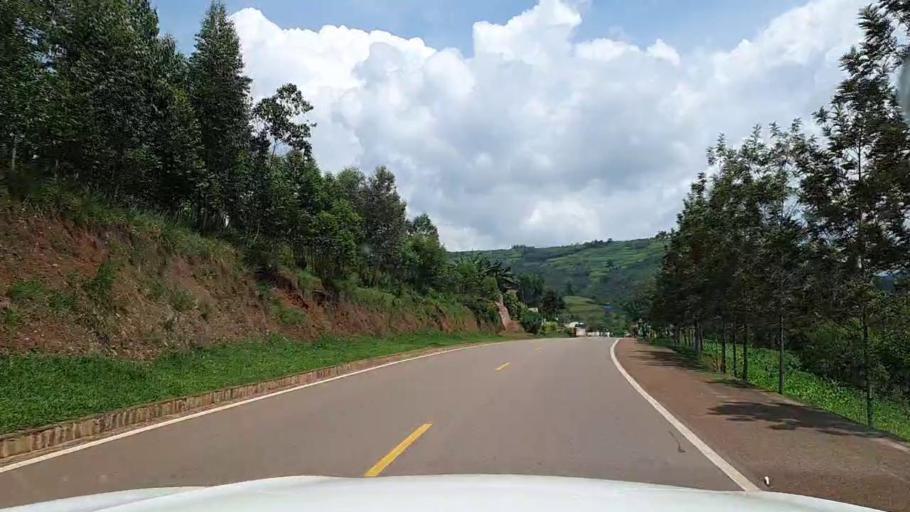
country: RW
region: Kigali
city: Kigali
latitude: -1.8275
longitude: 30.0788
